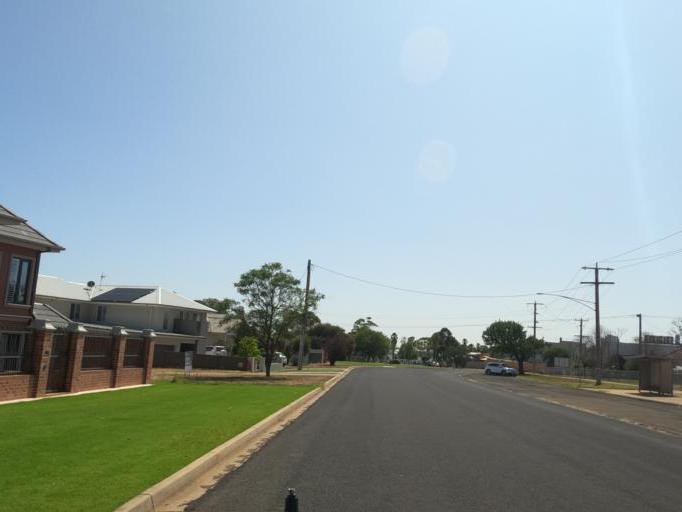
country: AU
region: Victoria
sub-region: Moira
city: Yarrawonga
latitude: -36.0095
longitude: 146.0019
